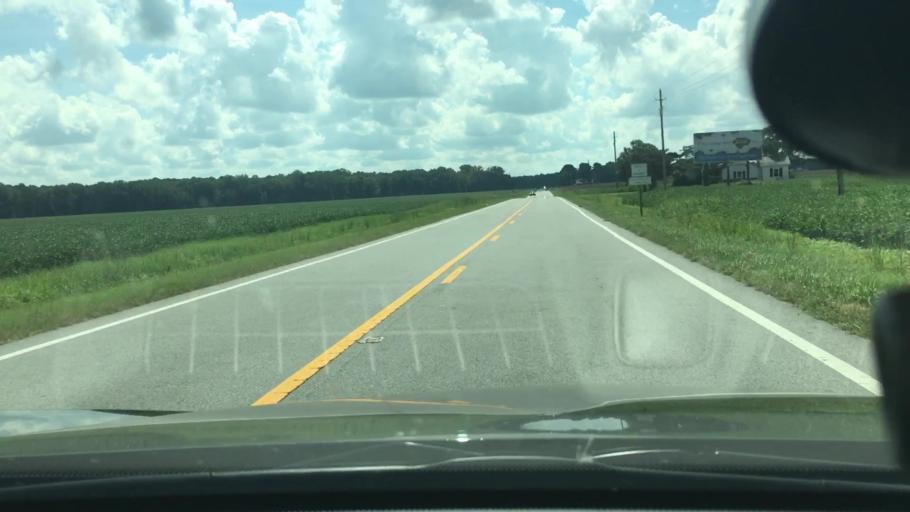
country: US
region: North Carolina
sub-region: Pitt County
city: Summerfield
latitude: 35.6553
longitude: -77.4683
